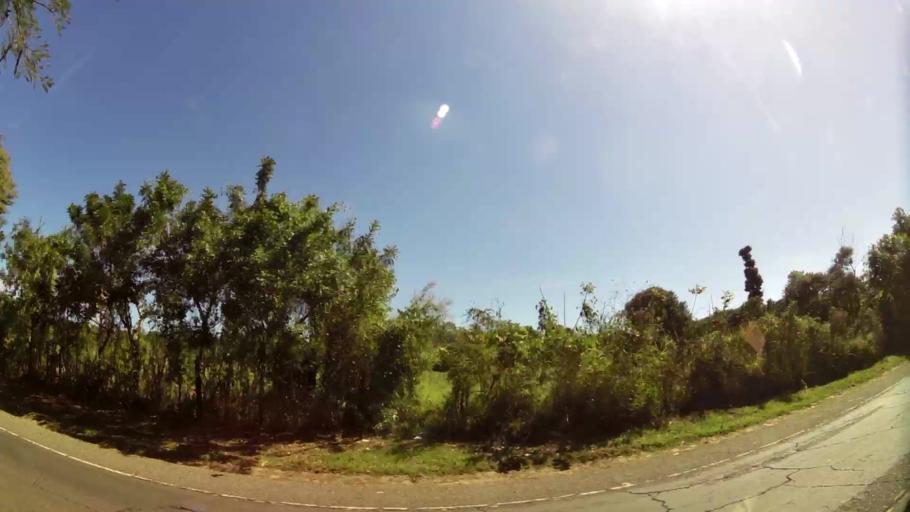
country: SV
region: Ahuachapan
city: Ahuachapan
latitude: 13.9479
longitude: -89.8393
